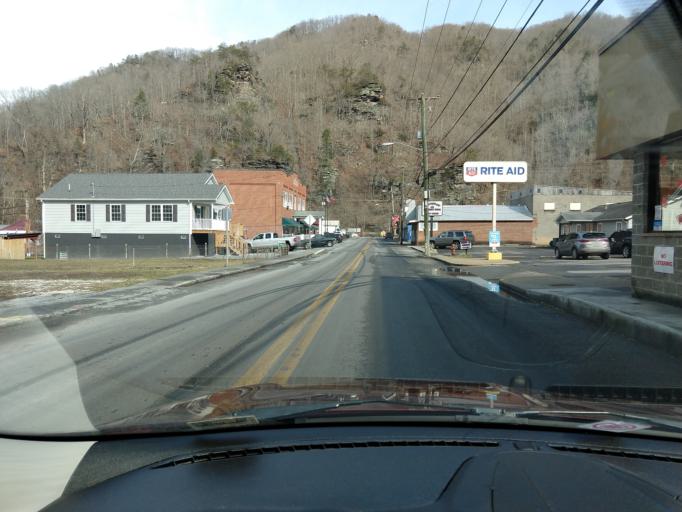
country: US
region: West Virginia
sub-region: McDowell County
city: Welch
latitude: 37.3518
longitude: -81.7991
